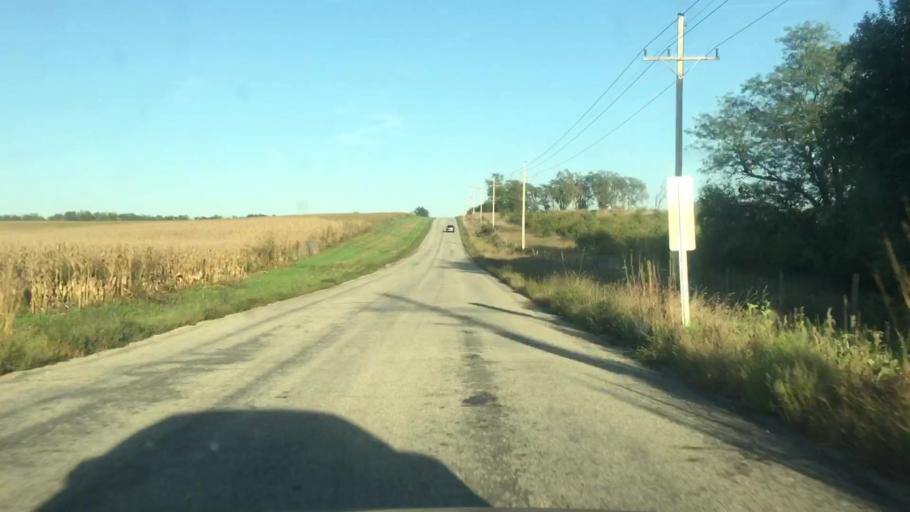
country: US
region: Kansas
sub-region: Atchison County
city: Atchison
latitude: 39.5656
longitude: -95.3339
